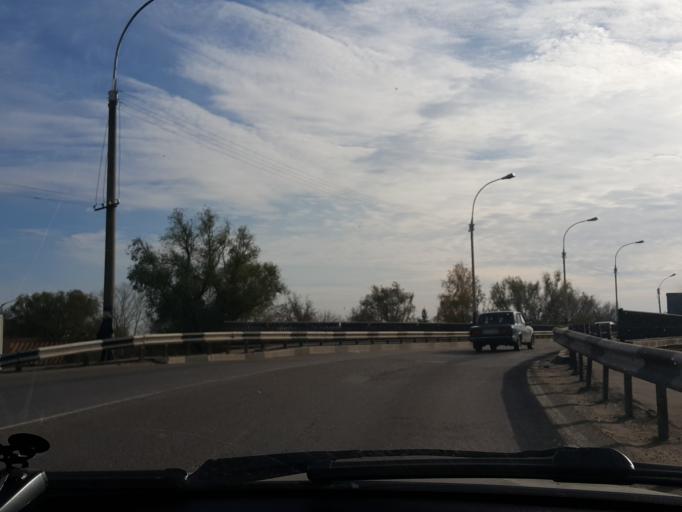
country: RU
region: Tambov
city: Tambov
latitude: 52.7277
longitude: 41.4642
